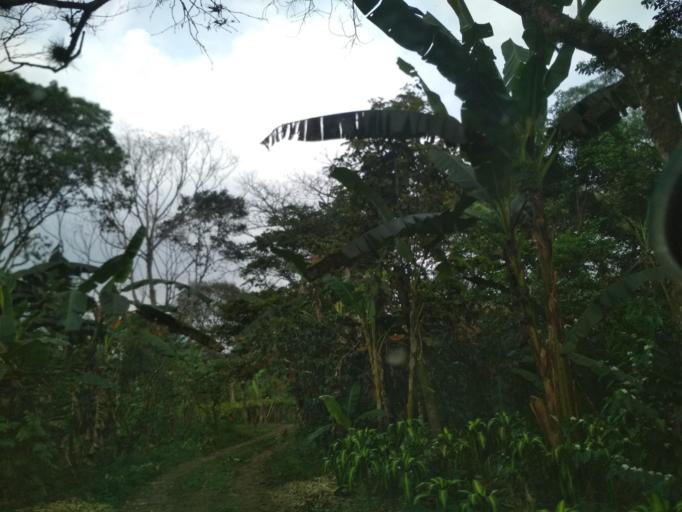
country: MX
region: Veracruz
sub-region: Cordoba
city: San Jose de Tapia
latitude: 18.8378
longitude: -96.9823
